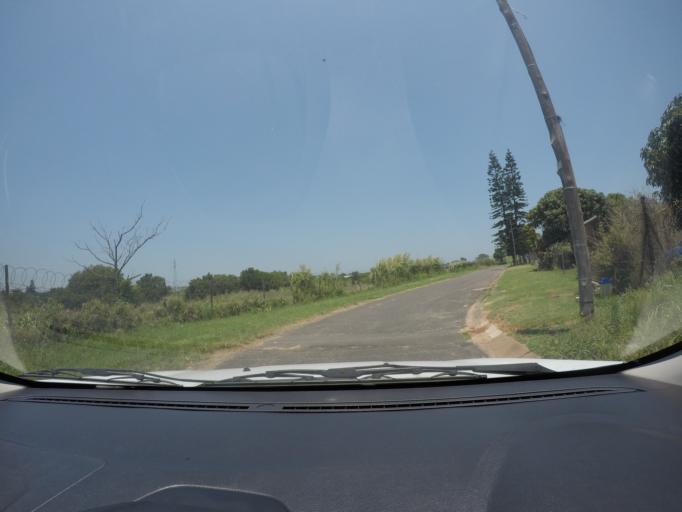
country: ZA
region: KwaZulu-Natal
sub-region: uThungulu District Municipality
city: eSikhawini
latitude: -28.8801
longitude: 31.8946
